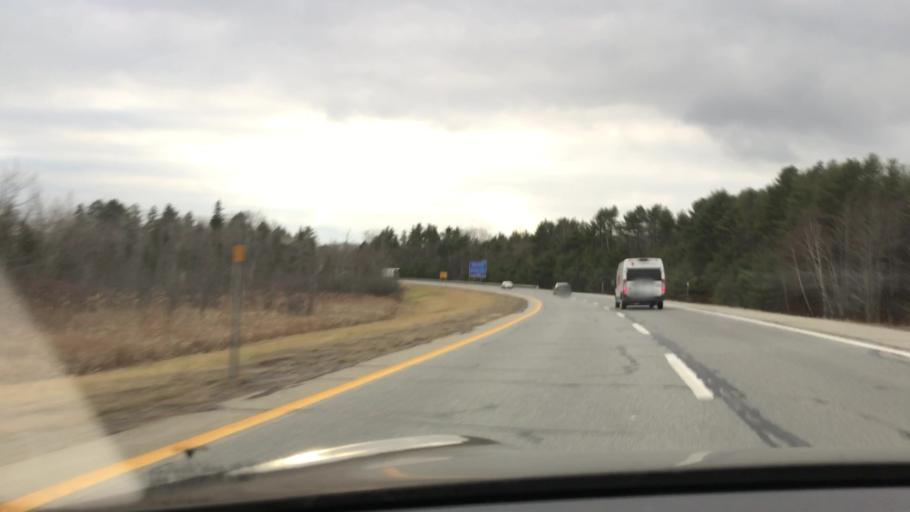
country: US
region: Maine
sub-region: Kennebec County
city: Gardiner
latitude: 44.2227
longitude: -69.8208
